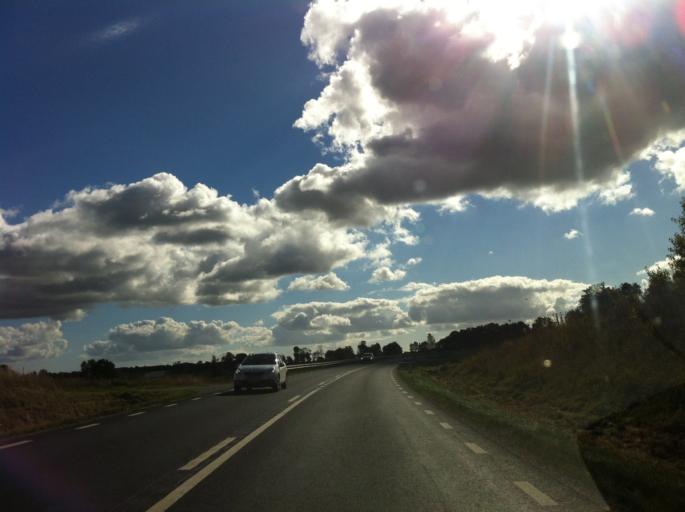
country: SE
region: Skane
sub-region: Tomelilla Kommun
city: Tomelilla
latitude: 55.6591
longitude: 14.0332
